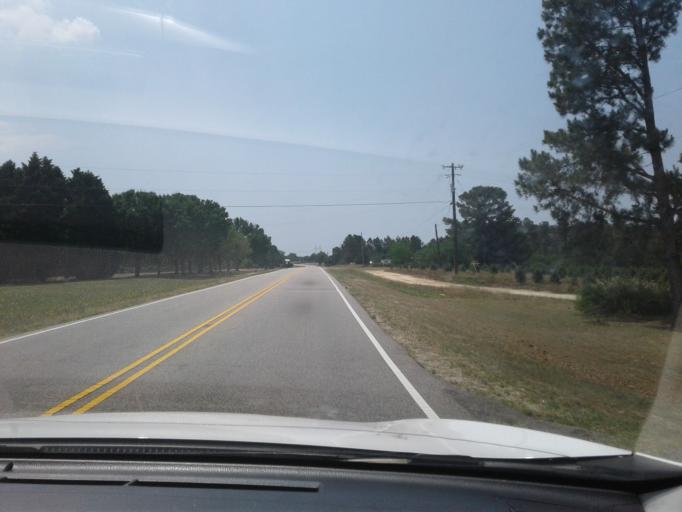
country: US
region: North Carolina
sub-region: Harnett County
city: Coats
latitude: 35.4475
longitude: -78.6859
